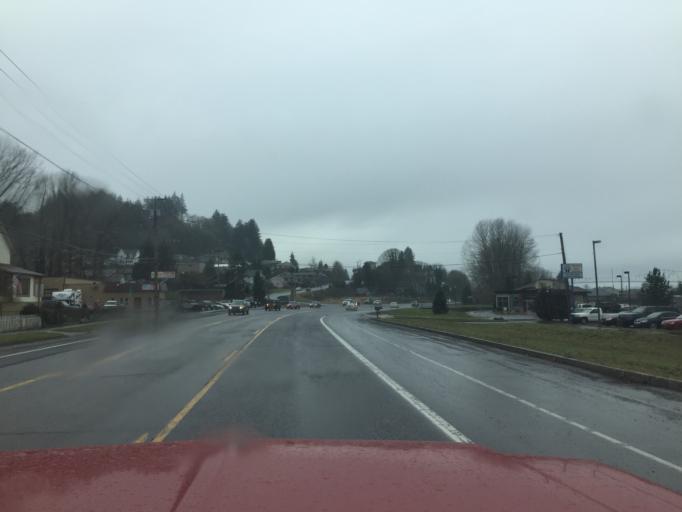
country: US
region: Oregon
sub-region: Columbia County
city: Rainier
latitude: 46.0901
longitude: -122.9410
